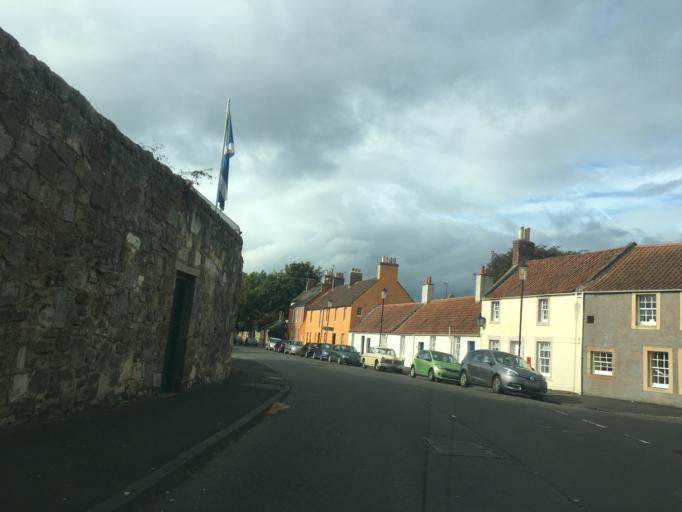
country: GB
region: Scotland
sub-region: East Lothian
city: Musselburgh
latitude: 55.9351
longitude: -3.0433
